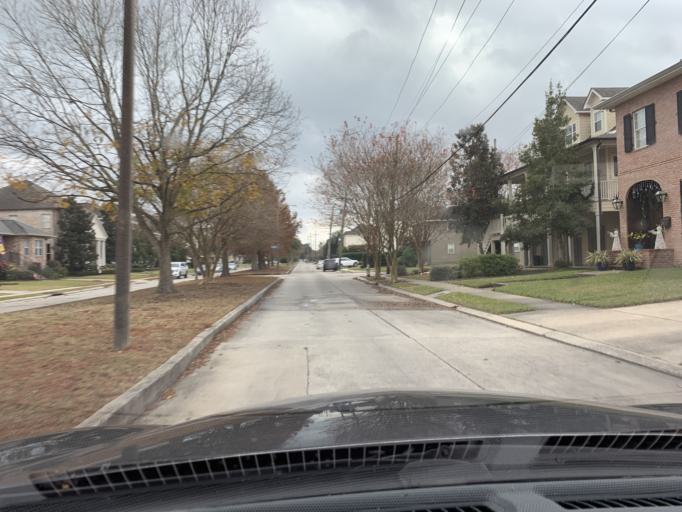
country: US
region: Louisiana
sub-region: Jefferson Parish
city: Metairie
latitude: 30.0185
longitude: -90.1011
